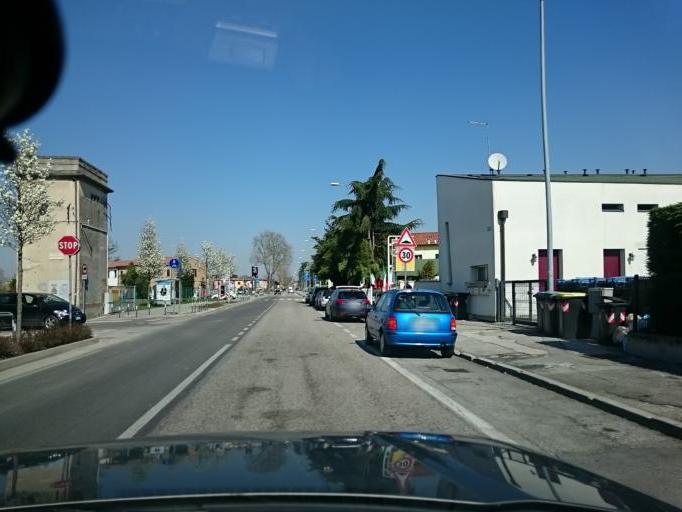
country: IT
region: Veneto
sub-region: Provincia di Padova
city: Albignasego
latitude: 45.3752
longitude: 11.8867
